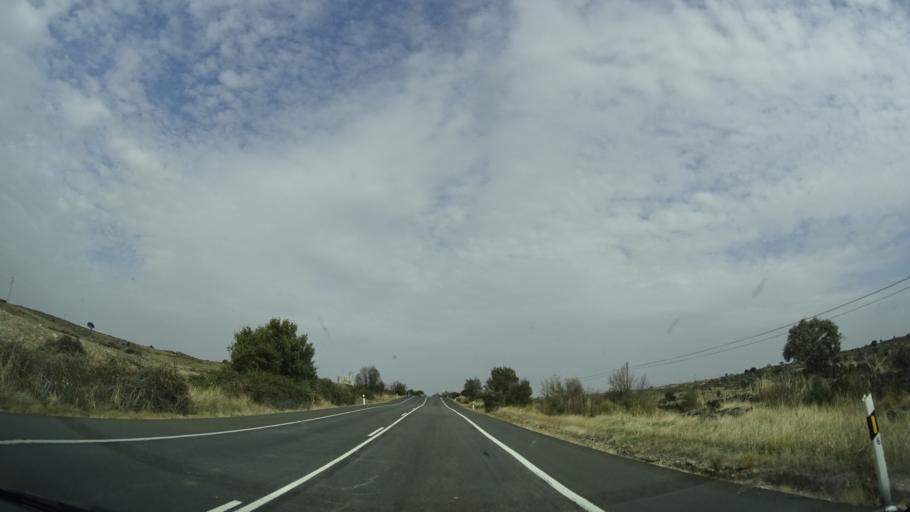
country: ES
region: Extremadura
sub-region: Provincia de Caceres
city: Trujillo
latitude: 39.4419
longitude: -5.8857
